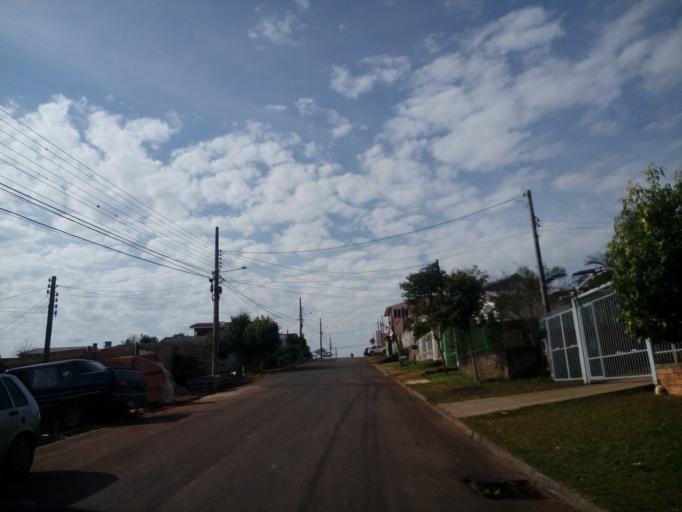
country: BR
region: Santa Catarina
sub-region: Chapeco
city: Chapeco
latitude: -27.1193
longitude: -52.6236
